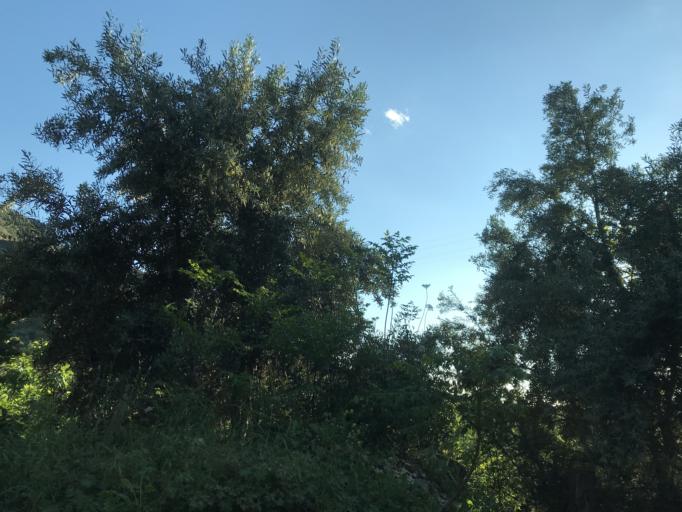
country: TR
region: Hatay
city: Samandag
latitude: 36.0785
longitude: 36.0205
